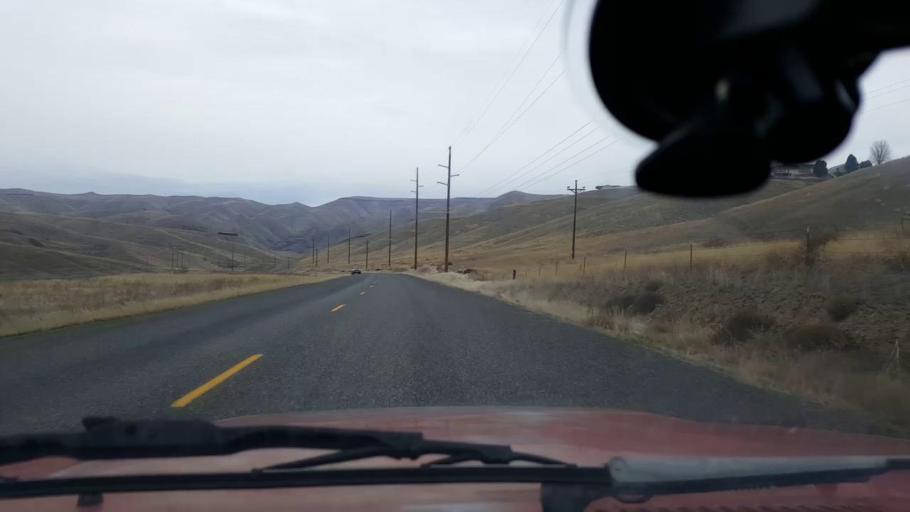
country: US
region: Washington
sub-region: Asotin County
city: Clarkston Heights-Vineland
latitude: 46.4037
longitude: -117.1024
